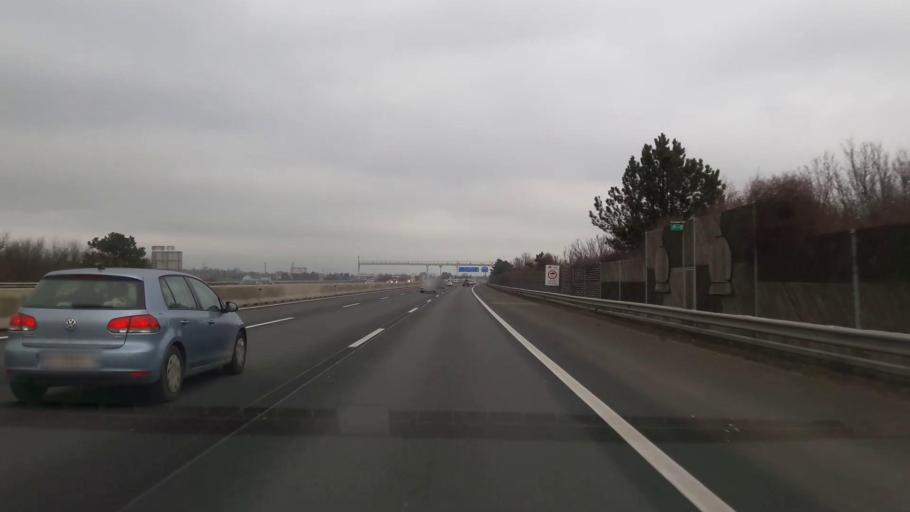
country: AT
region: Lower Austria
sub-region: Politischer Bezirk Baden
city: Kottingbrunn
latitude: 47.9457
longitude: 16.2150
